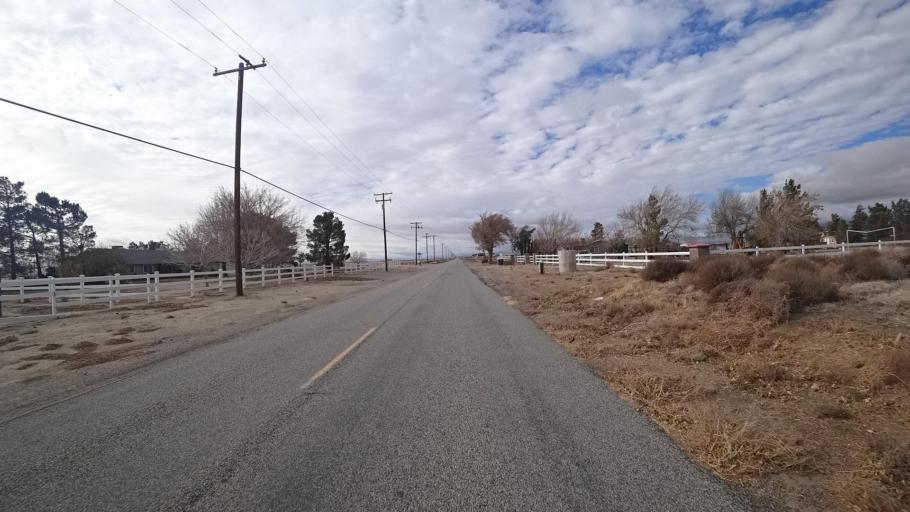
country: US
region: California
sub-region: Kern County
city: Rosamond
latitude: 34.8201
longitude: -118.2716
